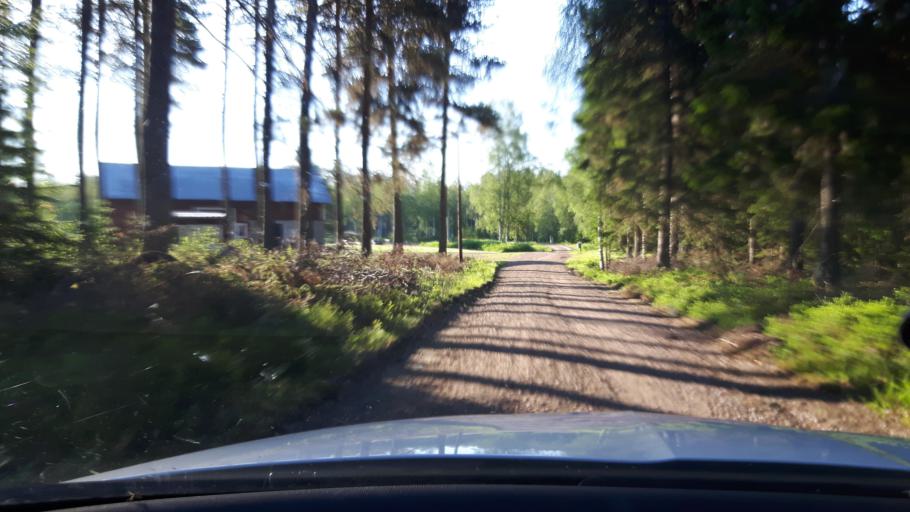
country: SE
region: Vaesternorrland
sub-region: Ange Kommun
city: Ange
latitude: 62.1827
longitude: 15.6277
